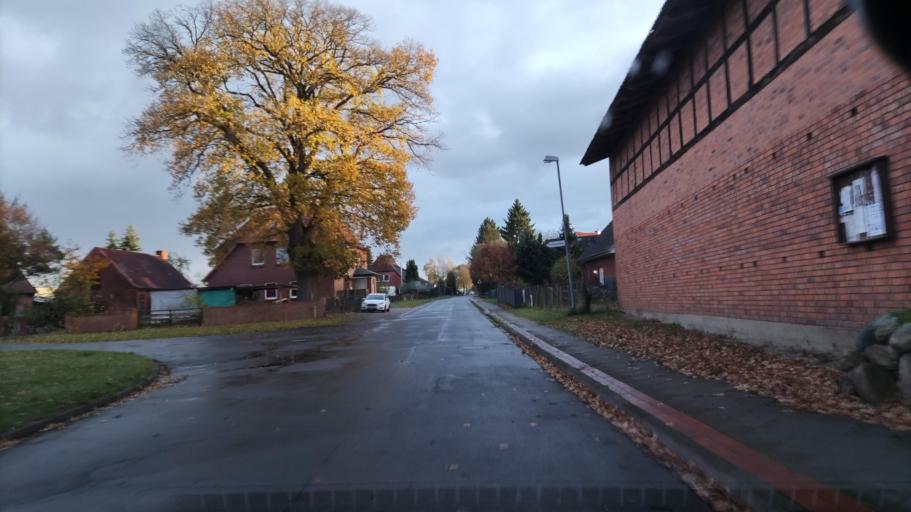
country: DE
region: Lower Saxony
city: Tosterglope
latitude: 53.2412
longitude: 10.7815
